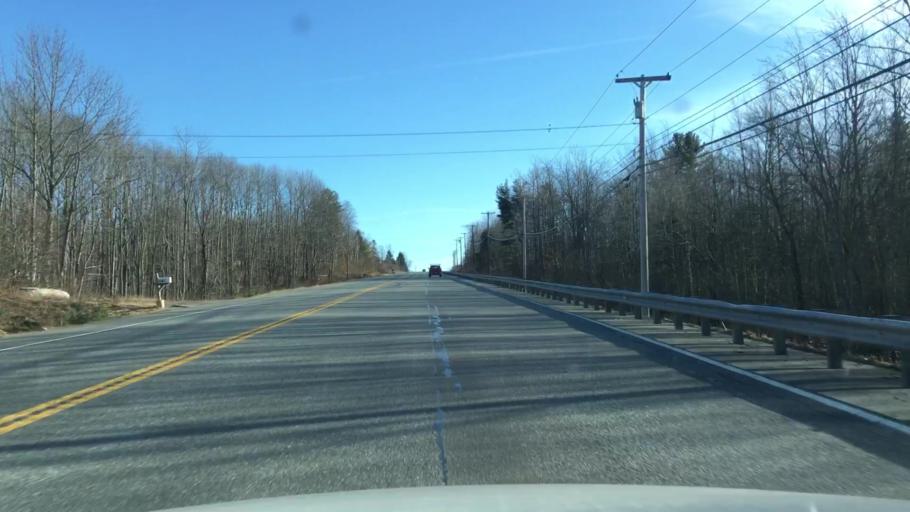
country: US
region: Maine
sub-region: Hancock County
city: Dedham
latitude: 44.6302
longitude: -68.5404
